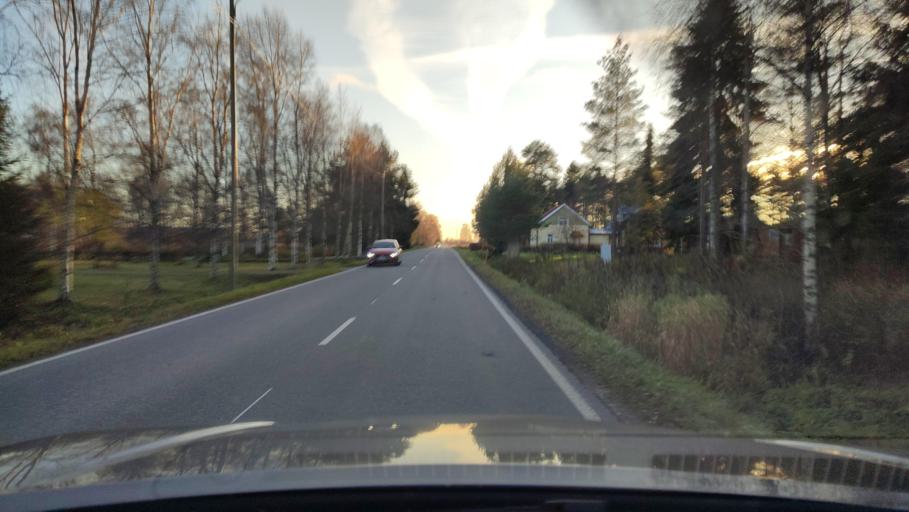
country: FI
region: Ostrobothnia
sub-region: Sydosterbotten
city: Naerpes
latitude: 62.6430
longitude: 21.5047
